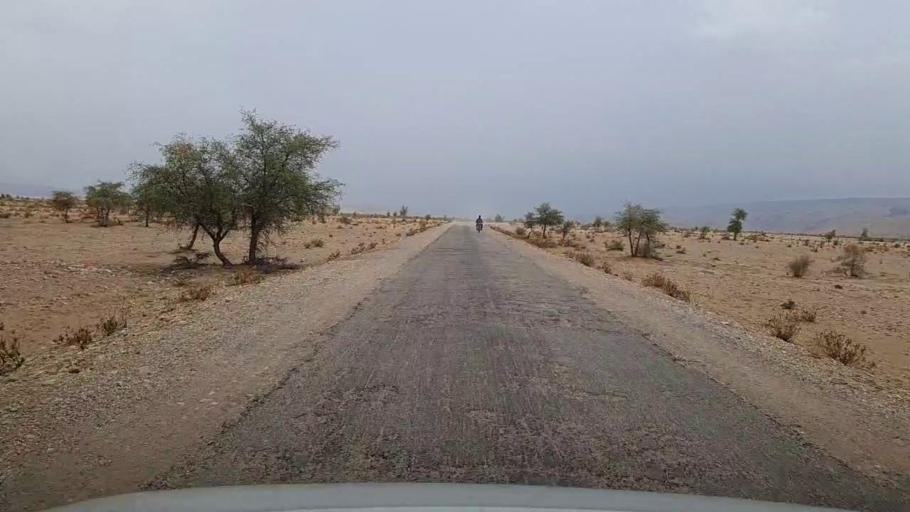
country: PK
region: Sindh
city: Sehwan
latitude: 26.2701
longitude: 67.7236
